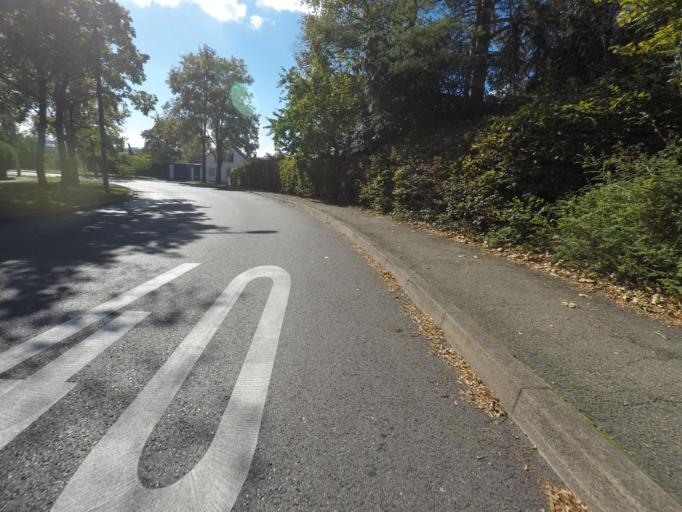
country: DE
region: Baden-Wuerttemberg
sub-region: Regierungsbezirk Stuttgart
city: Stuttgart
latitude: 48.7458
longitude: 9.1133
